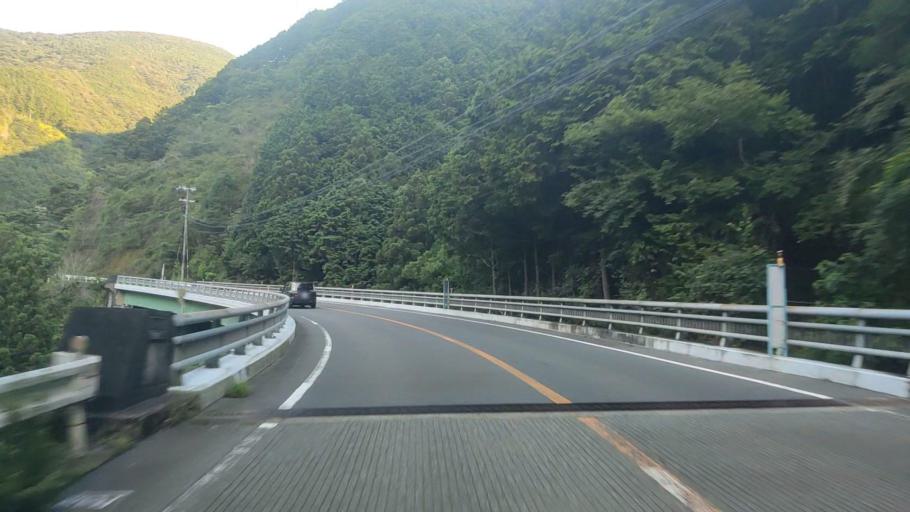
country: JP
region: Wakayama
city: Tanabe
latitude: 33.8147
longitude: 135.5613
